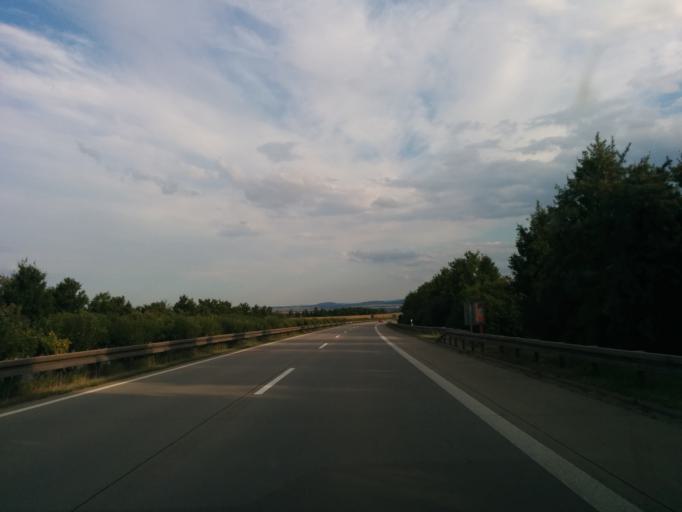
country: DE
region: Thuringia
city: Ingersleben
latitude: 50.9404
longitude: 10.9543
